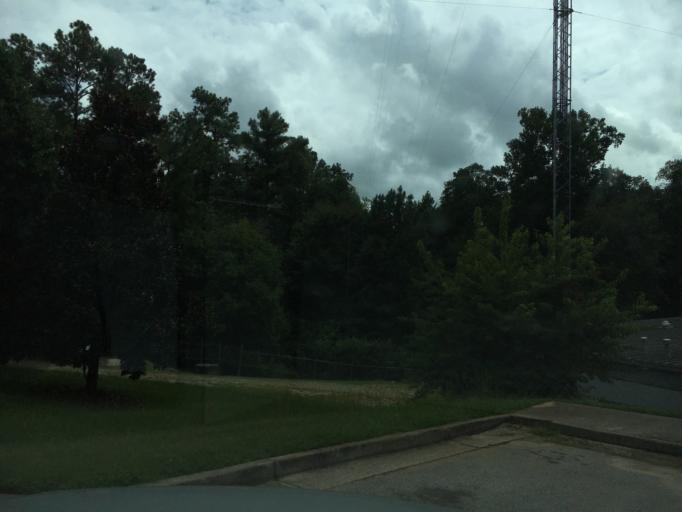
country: US
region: Georgia
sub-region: Rockdale County
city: Lakeview Estates
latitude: 33.6999
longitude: -84.0406
